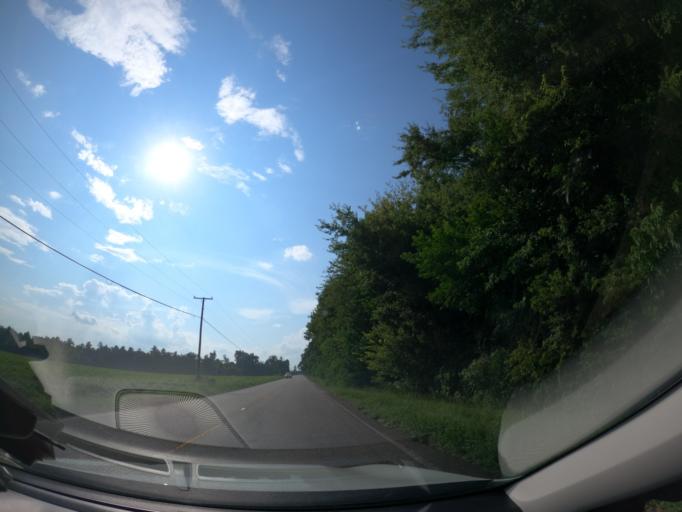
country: US
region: South Carolina
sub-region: Aiken County
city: Clearwater
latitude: 33.4208
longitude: -81.8536
